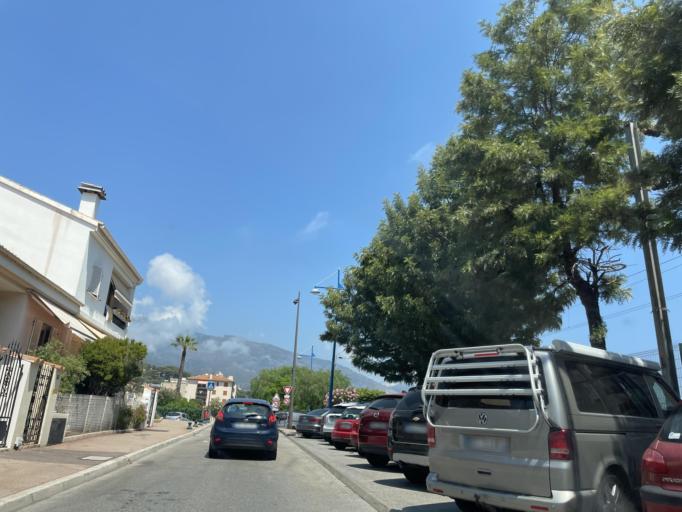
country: FR
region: Provence-Alpes-Cote d'Azur
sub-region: Departement des Alpes-Maritimes
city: Roquebrune-Cap-Martin
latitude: 43.7629
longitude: 7.4822
